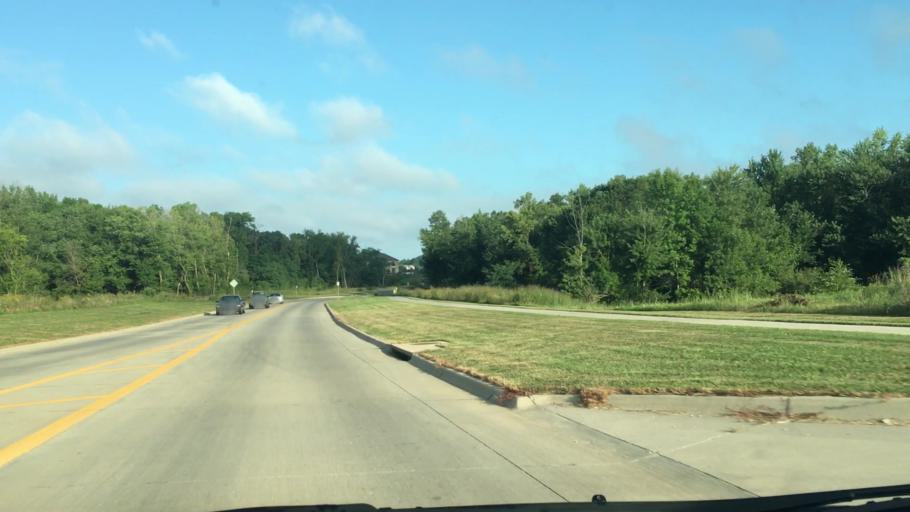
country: US
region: Iowa
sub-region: Johnson County
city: Coralville
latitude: 41.6993
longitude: -91.5476
